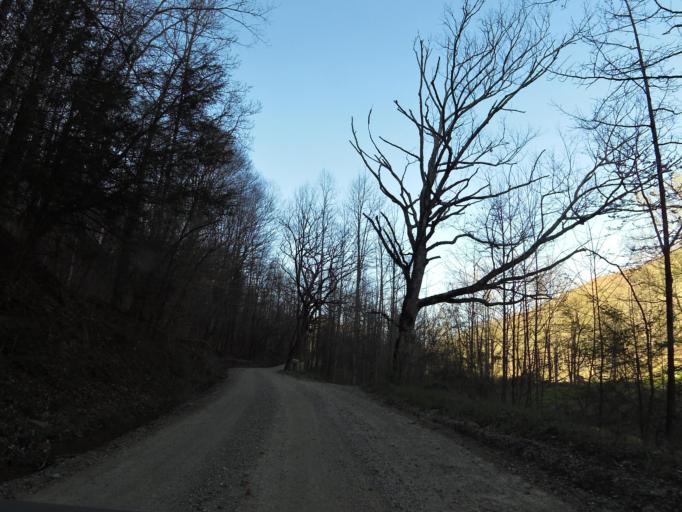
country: US
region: Tennessee
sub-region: Scott County
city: Huntsville
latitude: 36.2347
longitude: -84.4177
